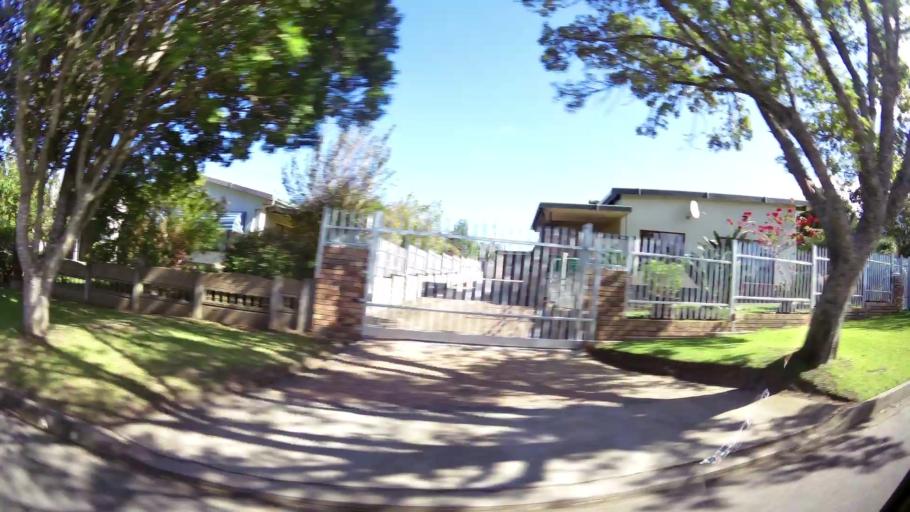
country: ZA
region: Western Cape
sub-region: Eden District Municipality
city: George
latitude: -33.9432
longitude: 22.4773
